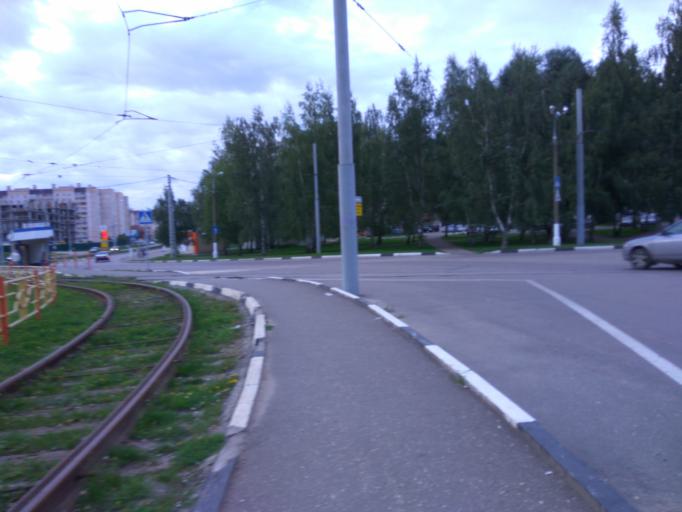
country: RU
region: Moskovskaya
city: Sychevo
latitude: 55.0561
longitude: 38.7490
